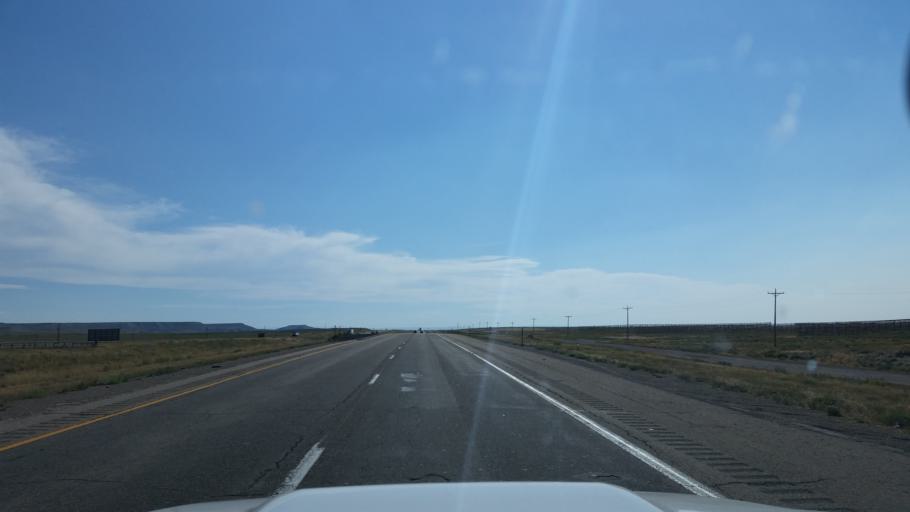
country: US
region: Wyoming
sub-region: Uinta County
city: Lyman
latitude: 41.4614
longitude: -110.0552
